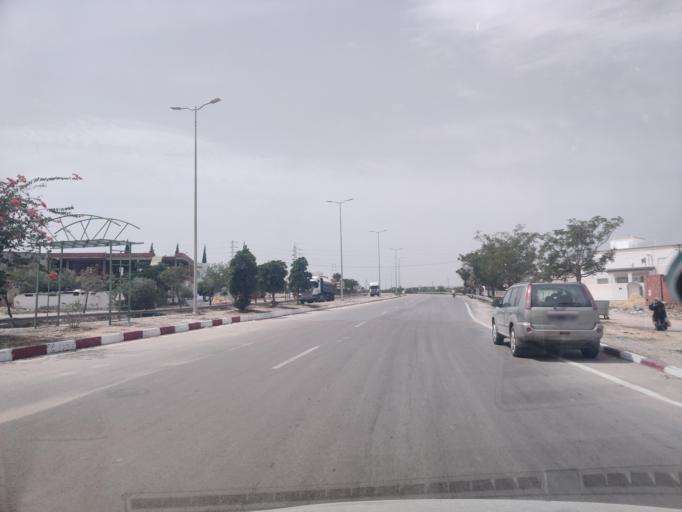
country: TN
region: Susah
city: Akouda
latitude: 35.8358
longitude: 10.5586
